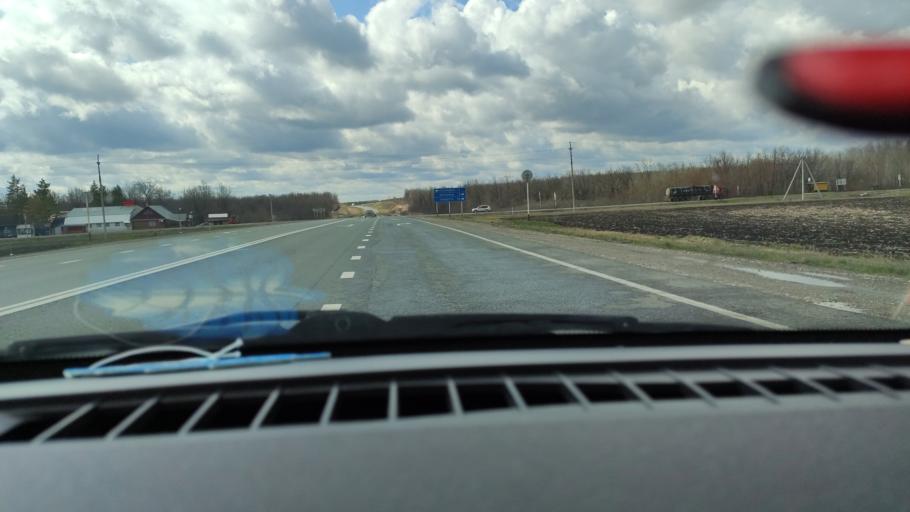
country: RU
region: Samara
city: Yelkhovka
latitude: 53.7609
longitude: 50.2257
